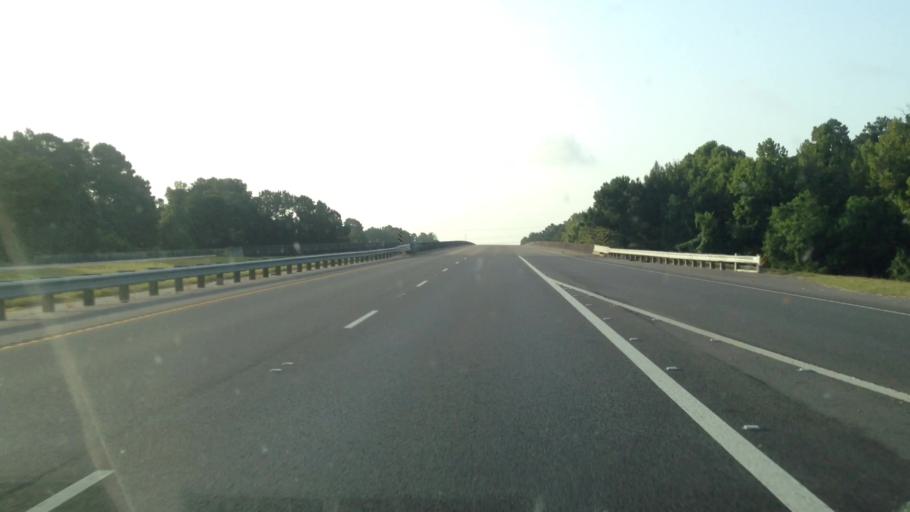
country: US
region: Louisiana
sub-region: Rapides Parish
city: Boyce
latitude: 31.4075
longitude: -92.7144
